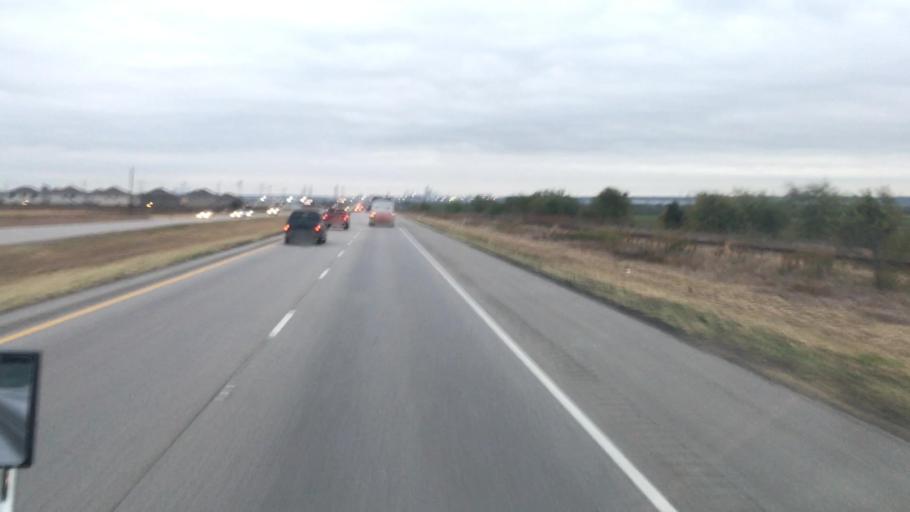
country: US
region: Texas
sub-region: Johnson County
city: Venus
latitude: 32.4388
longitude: -97.0937
